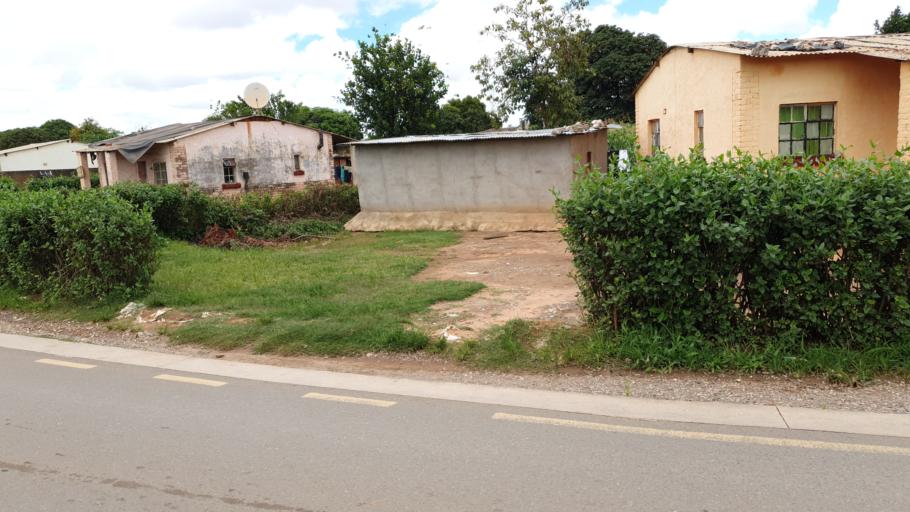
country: ZM
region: Lusaka
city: Lusaka
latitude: -15.4261
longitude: 28.3053
